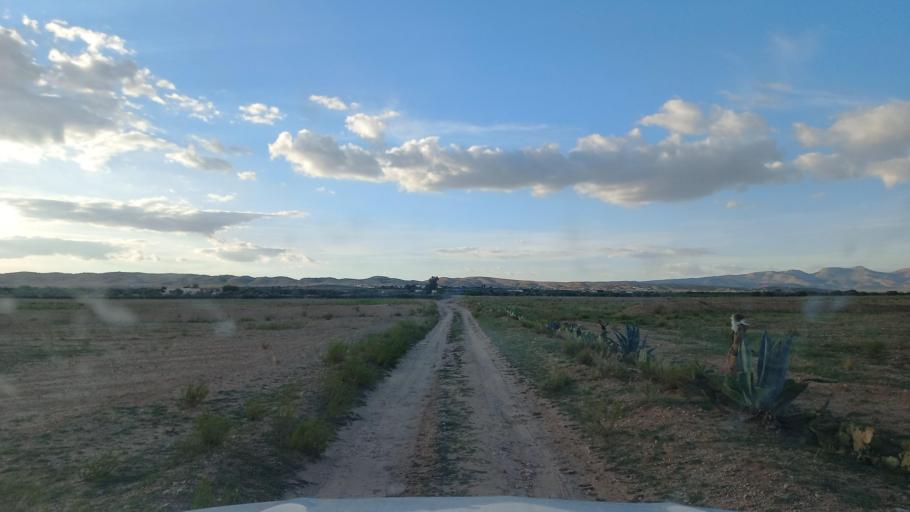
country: TN
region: Al Qasrayn
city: Sbiba
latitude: 35.3524
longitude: 9.0267
